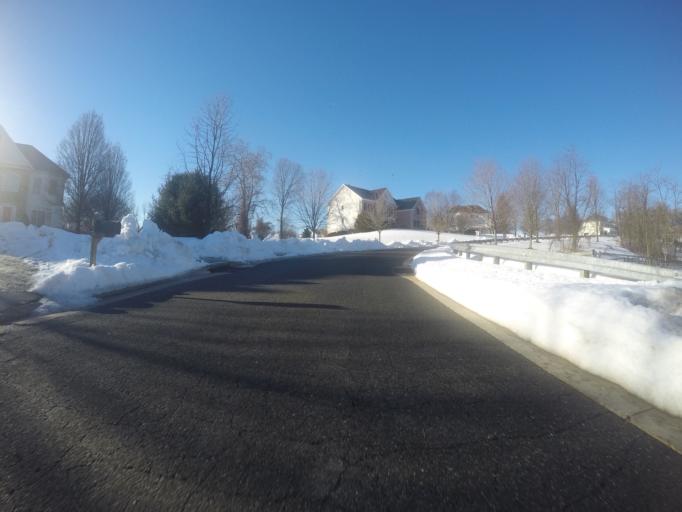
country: US
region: Maryland
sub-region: Baltimore County
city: Hunt Valley
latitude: 39.5319
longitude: -76.6386
